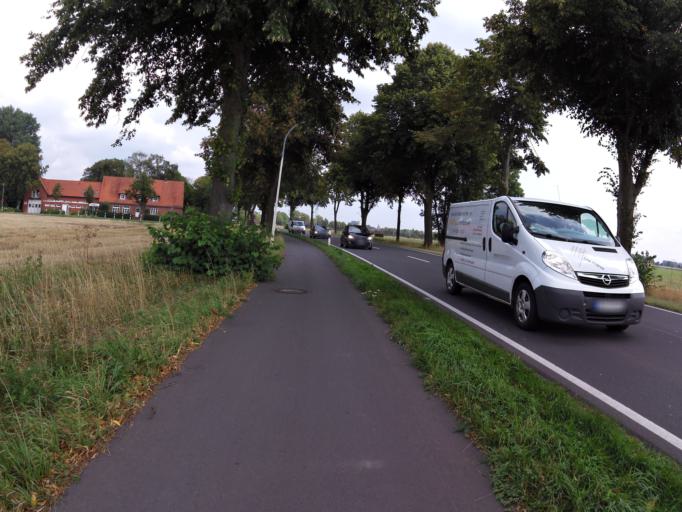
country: DE
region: Lower Saxony
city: Verden
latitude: 52.9214
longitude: 9.1997
